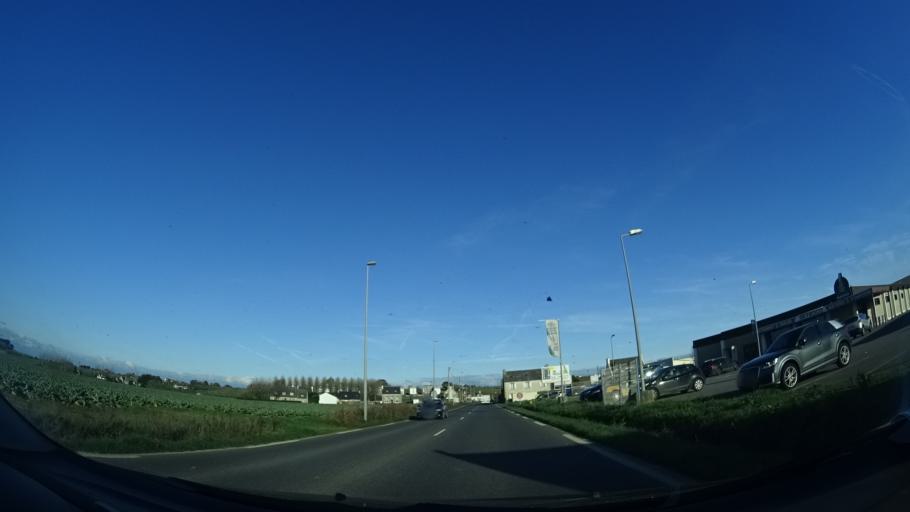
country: FR
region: Brittany
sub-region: Departement du Finistere
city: Saint-Pol-de-Leon
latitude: 48.6796
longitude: -4.0045
